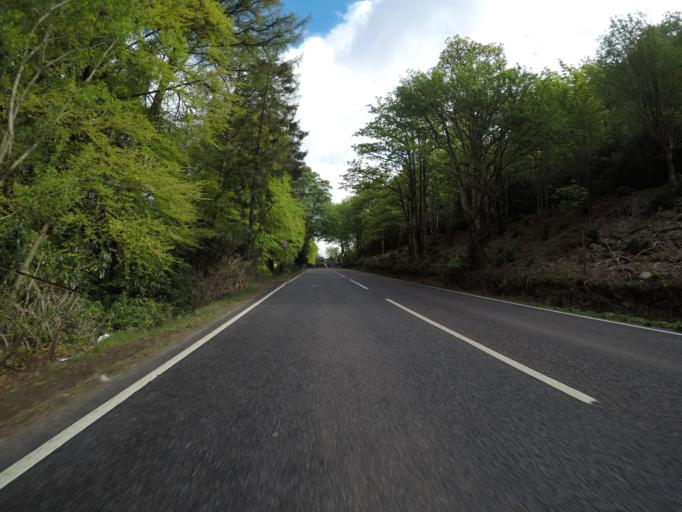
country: GB
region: Scotland
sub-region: Highland
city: Spean Bridge
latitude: 56.9566
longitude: -4.9099
